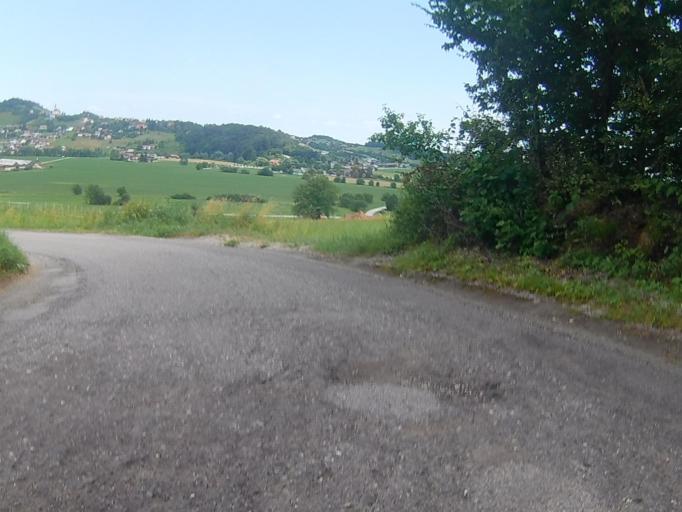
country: SI
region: Pesnica
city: Pesnica pri Mariboru
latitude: 46.6033
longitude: 15.6397
